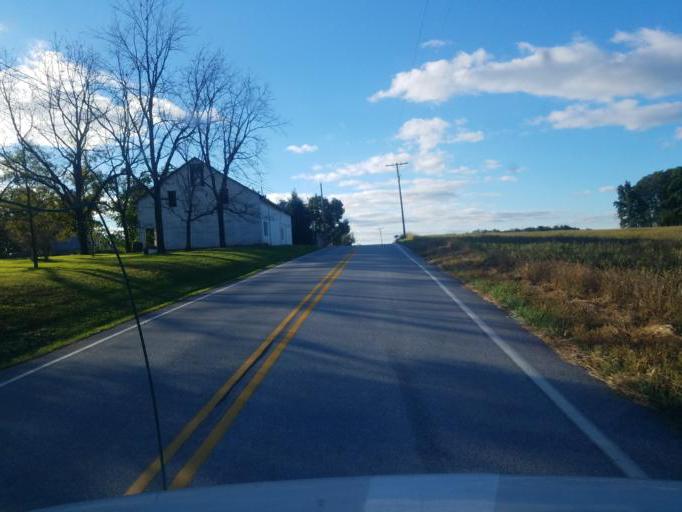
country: US
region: Pennsylvania
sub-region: Adams County
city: Gettysburg
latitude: 39.8713
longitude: -77.2302
